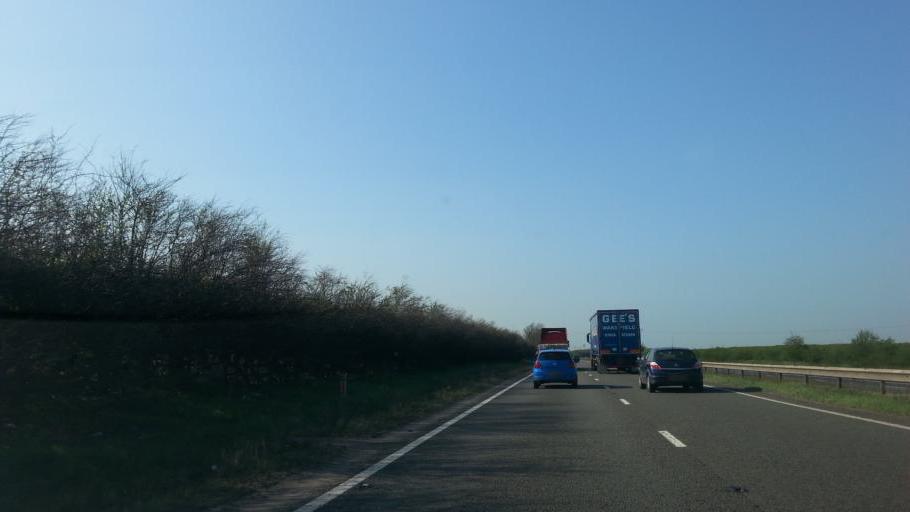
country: GB
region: England
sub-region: Lincolnshire
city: Long Bennington
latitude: 53.0343
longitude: -0.7731
